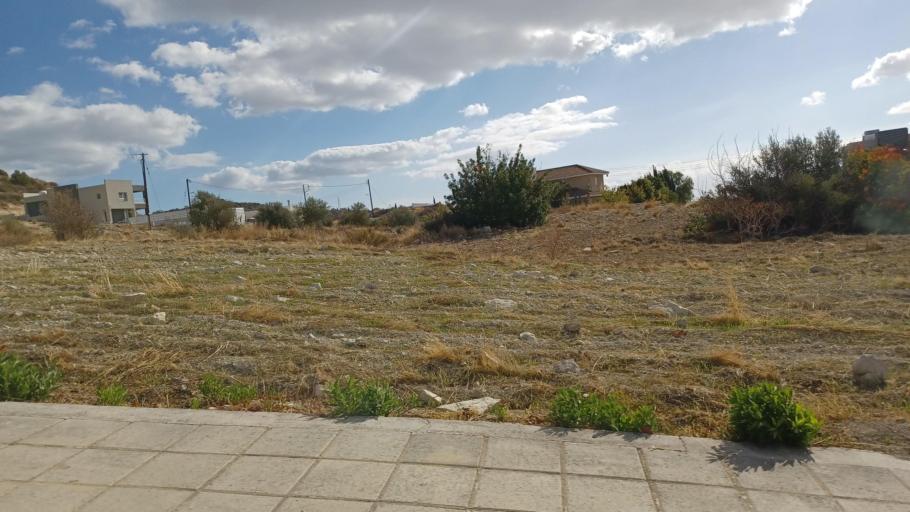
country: CY
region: Limassol
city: Pano Polemidia
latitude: 34.7413
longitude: 33.0099
